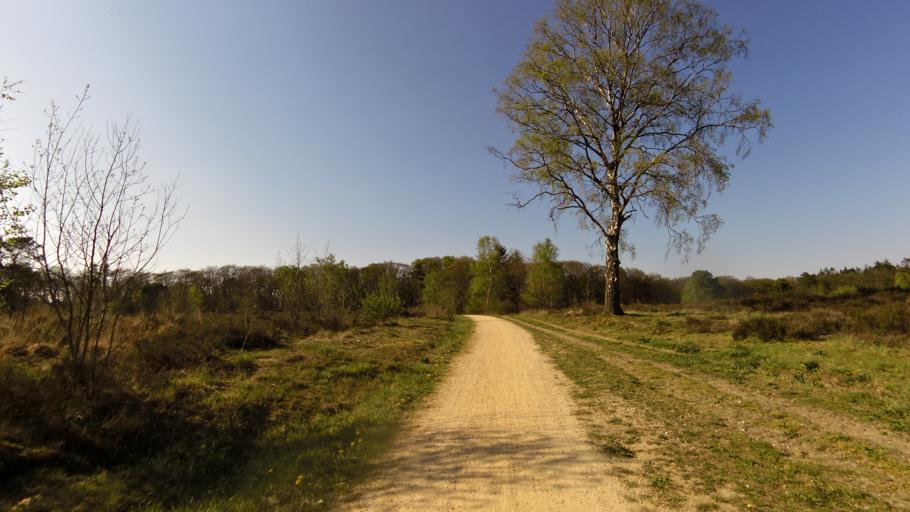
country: NL
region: Gelderland
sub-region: Gemeente Arnhem
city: Hoogkamp
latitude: 52.0181
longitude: 5.8688
